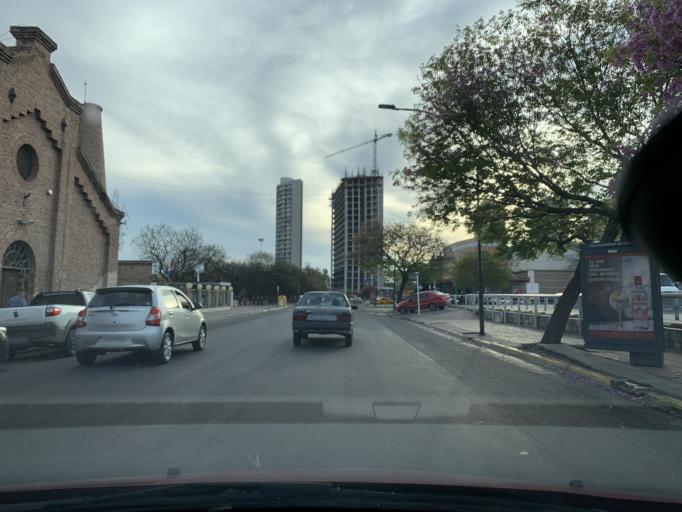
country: AR
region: Cordoba
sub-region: Departamento de Capital
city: Cordoba
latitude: -31.4089
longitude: -64.1697
